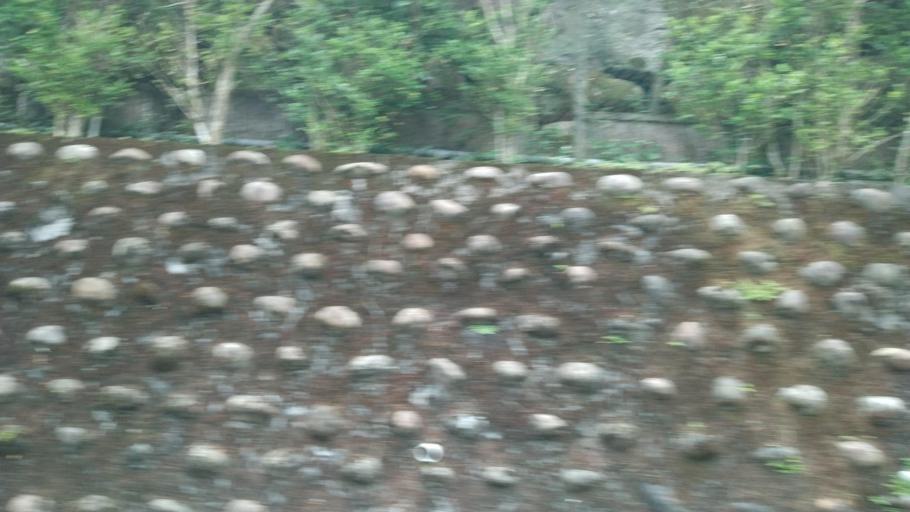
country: TW
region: Taipei
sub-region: Taipei
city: Banqiao
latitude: 24.9205
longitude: 121.4253
